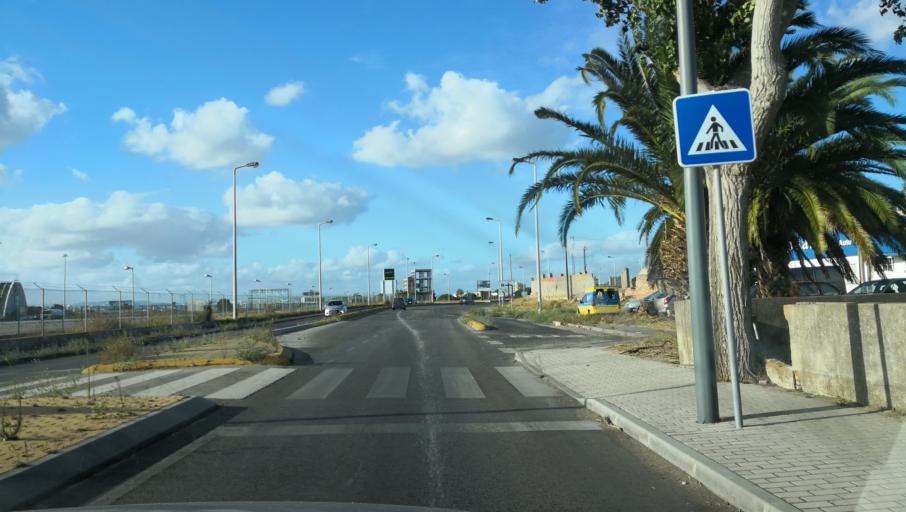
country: PT
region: Setubal
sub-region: Barreiro
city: Barreiro
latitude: 38.6677
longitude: -9.0569
